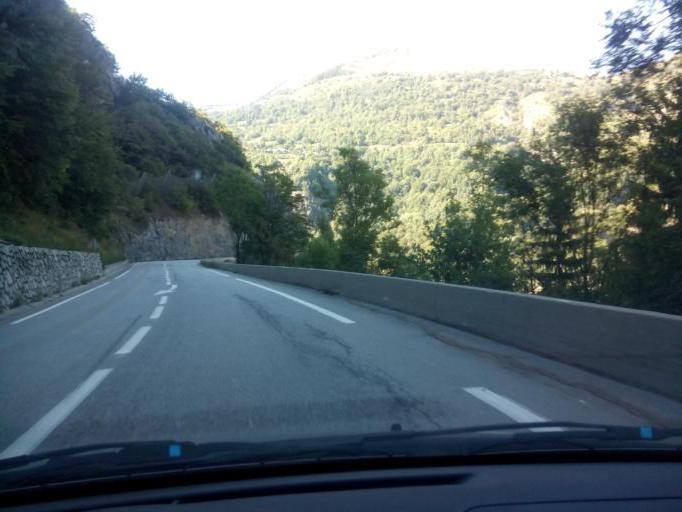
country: FR
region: Rhone-Alpes
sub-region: Departement de l'Isere
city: Mont-de-Lans
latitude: 45.0388
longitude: 6.1012
